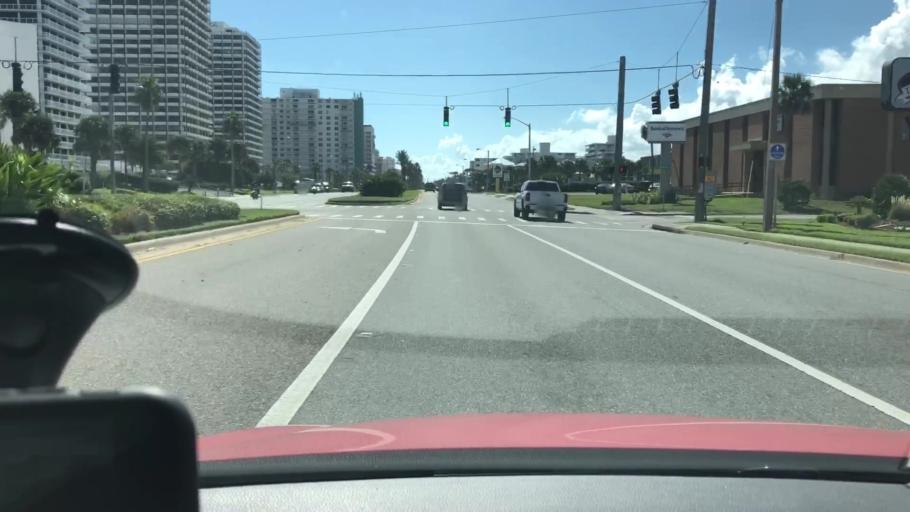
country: US
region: Florida
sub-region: Volusia County
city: Holly Hill
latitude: 29.2695
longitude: -81.0293
